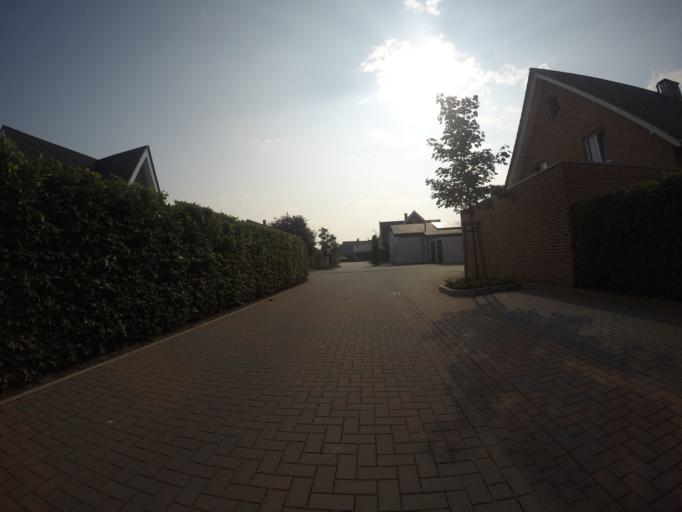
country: DE
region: North Rhine-Westphalia
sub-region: Regierungsbezirk Munster
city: Isselburg
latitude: 51.8197
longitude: 6.5045
